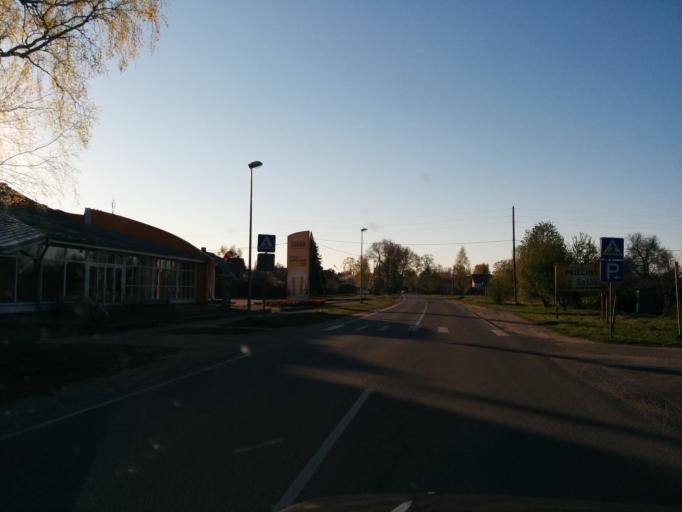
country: LV
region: Engure
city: Smarde
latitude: 57.0241
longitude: 23.4918
